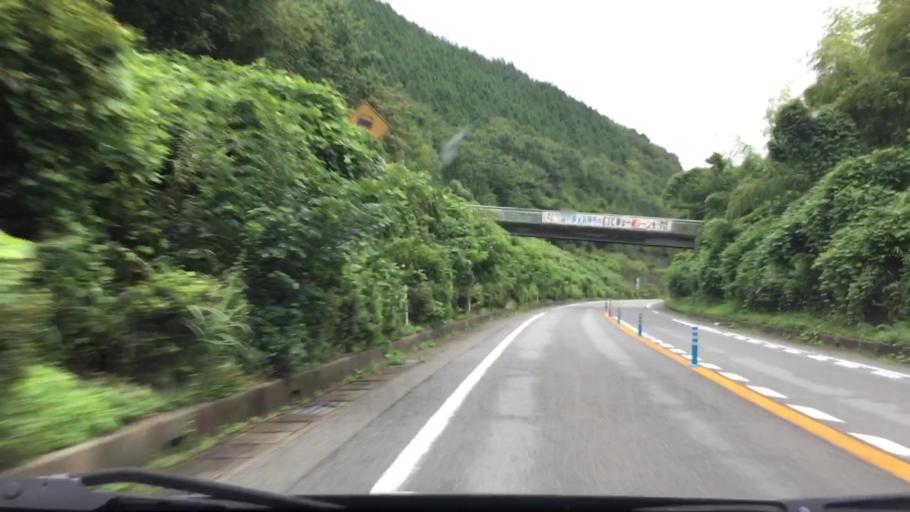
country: JP
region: Hyogo
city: Nishiwaki
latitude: 35.0397
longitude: 134.7696
